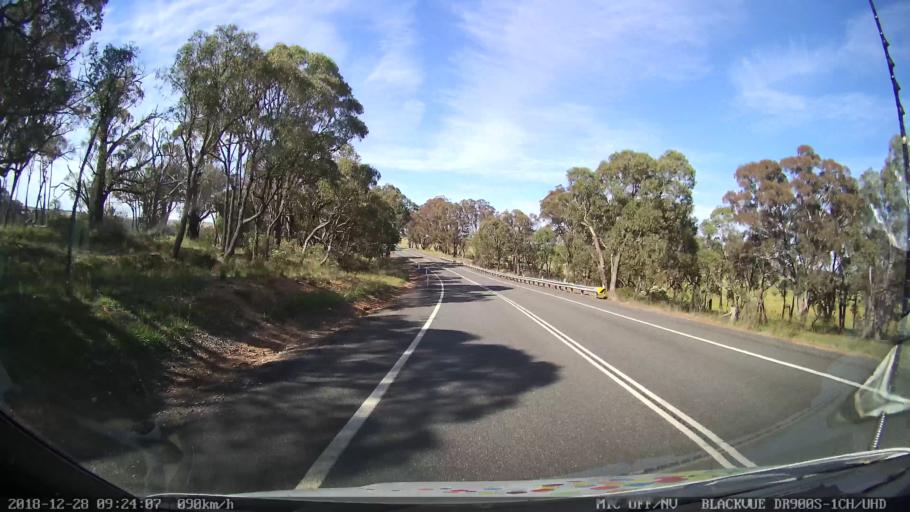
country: AU
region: New South Wales
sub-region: Upper Lachlan Shire
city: Crookwell
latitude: -34.3937
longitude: 149.3814
